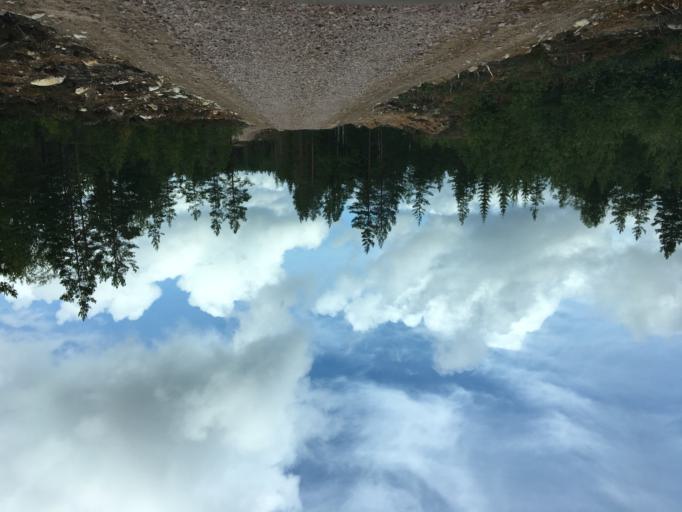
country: SE
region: OErebro
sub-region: Hallefors Kommun
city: Haellefors
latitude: 60.0717
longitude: 14.4754
